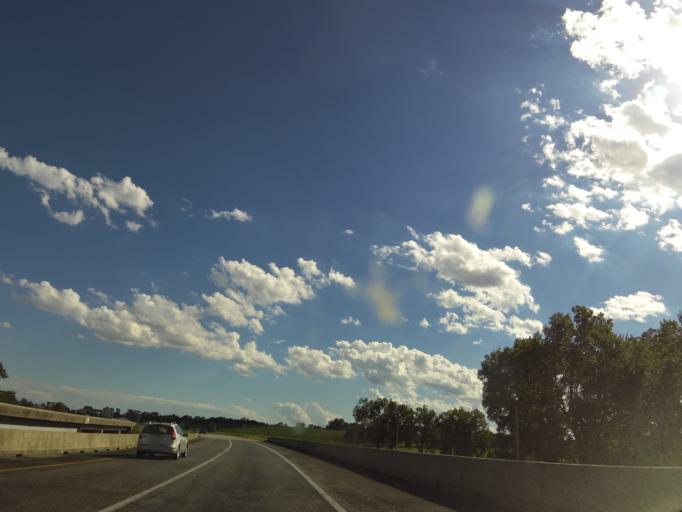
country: US
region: Illinois
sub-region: Adams County
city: Quincy
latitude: 39.9319
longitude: -91.5223
